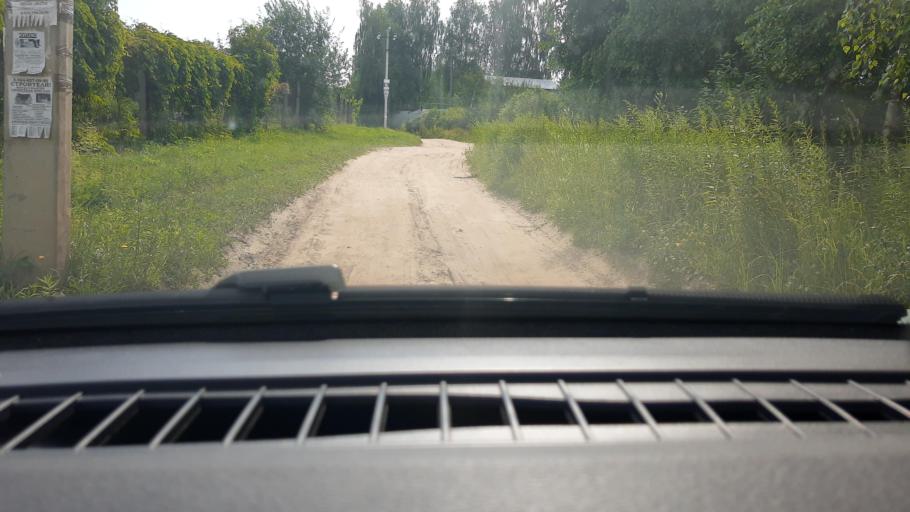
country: RU
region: Nizjnij Novgorod
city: Neklyudovo
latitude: 56.4279
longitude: 44.0014
